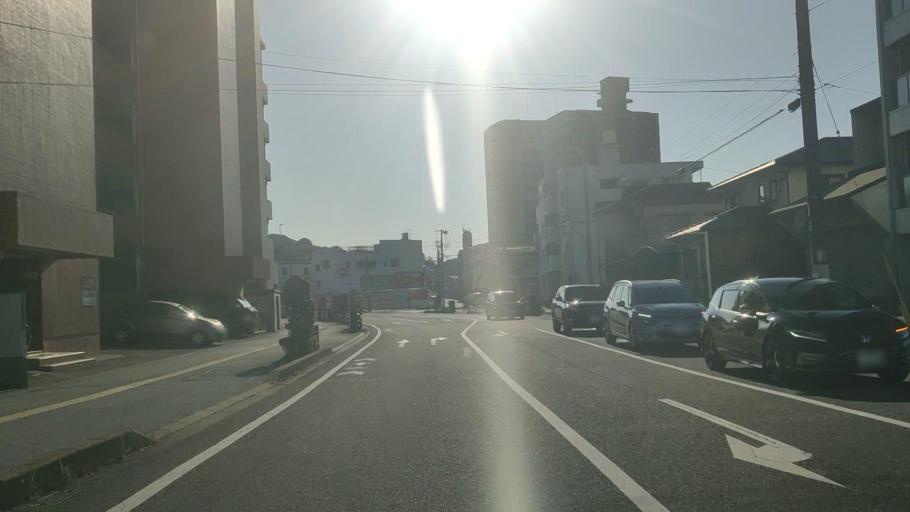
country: JP
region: Oita
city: Oita
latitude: 33.2307
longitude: 131.6017
